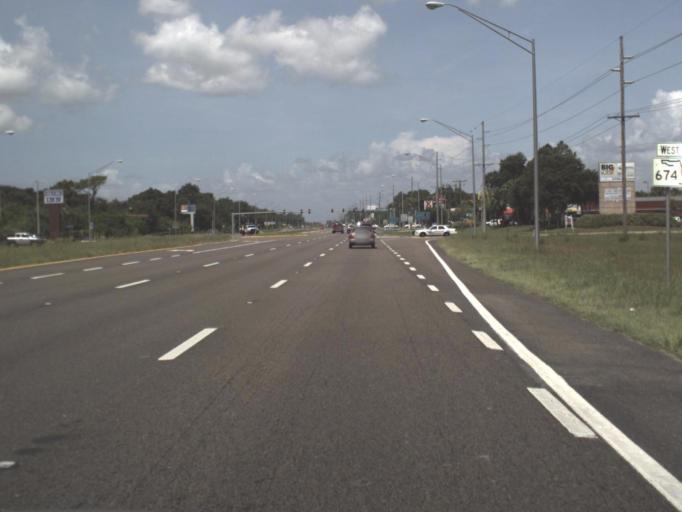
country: US
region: Florida
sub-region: Hillsborough County
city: Sun City Center
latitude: 27.7131
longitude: -82.3908
